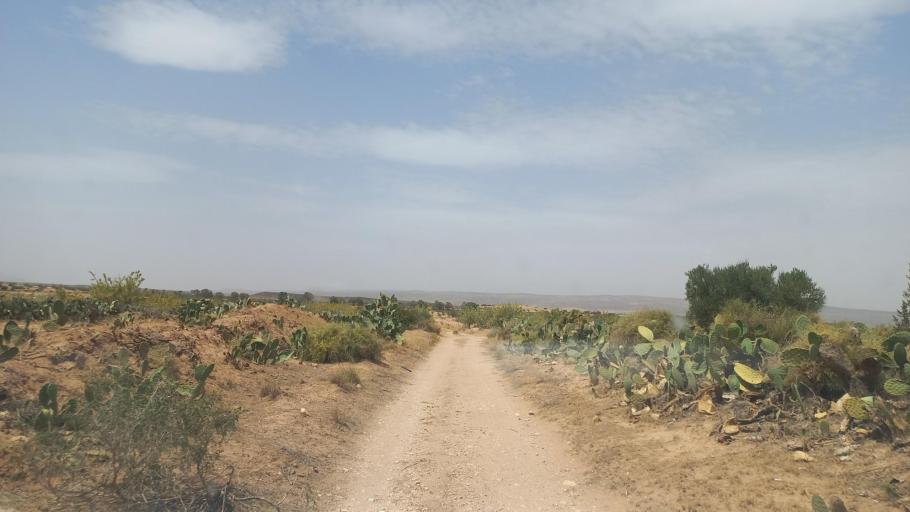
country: TN
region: Al Qasrayn
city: Kasserine
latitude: 35.2621
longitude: 8.9869
